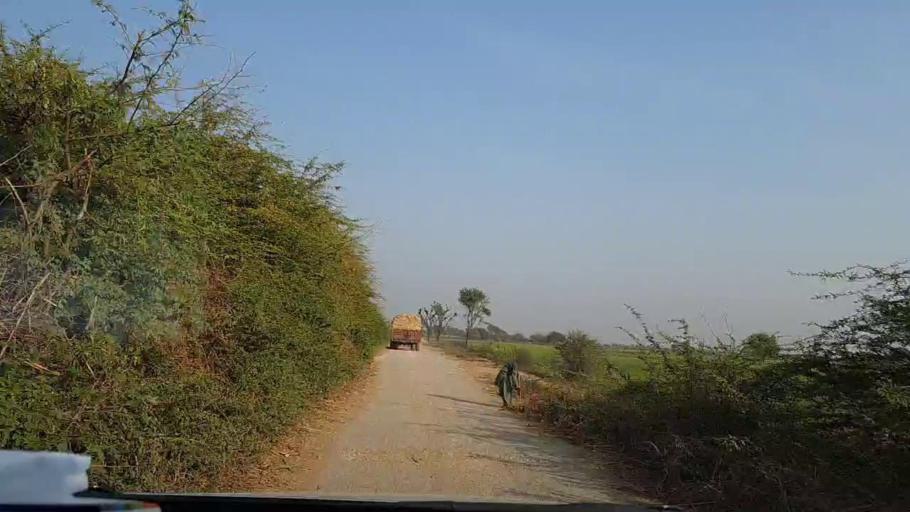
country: PK
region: Sindh
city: Tando Ghulam Ali
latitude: 25.2117
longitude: 68.8905
